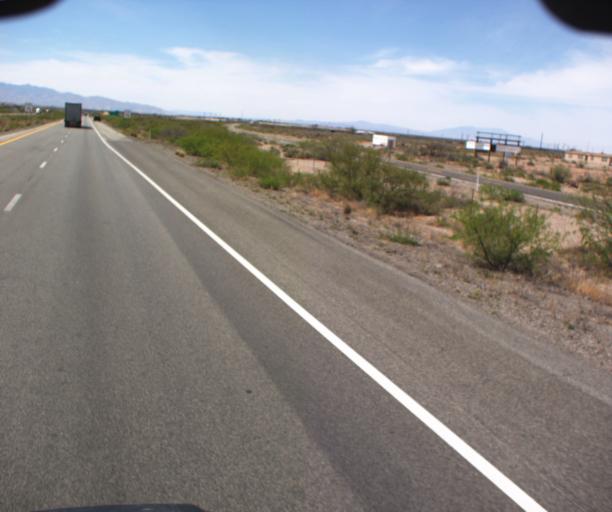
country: US
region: New Mexico
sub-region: Hidalgo County
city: Lordsburg
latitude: 32.2575
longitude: -109.1871
